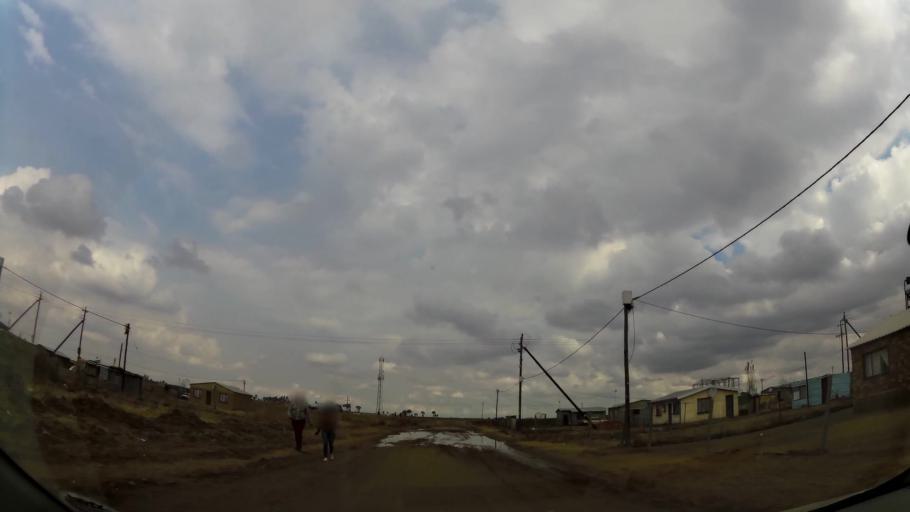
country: ZA
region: Orange Free State
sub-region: Fezile Dabi District Municipality
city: Sasolburg
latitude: -26.8653
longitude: 27.8945
